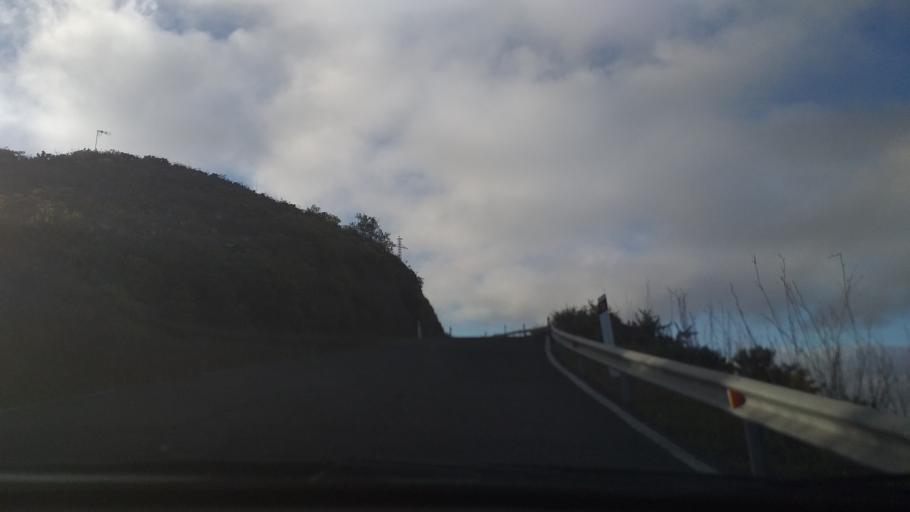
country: ES
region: Canary Islands
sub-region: Provincia de Las Palmas
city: Valsequillo de Gran Canaria
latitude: 27.9577
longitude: -15.4976
